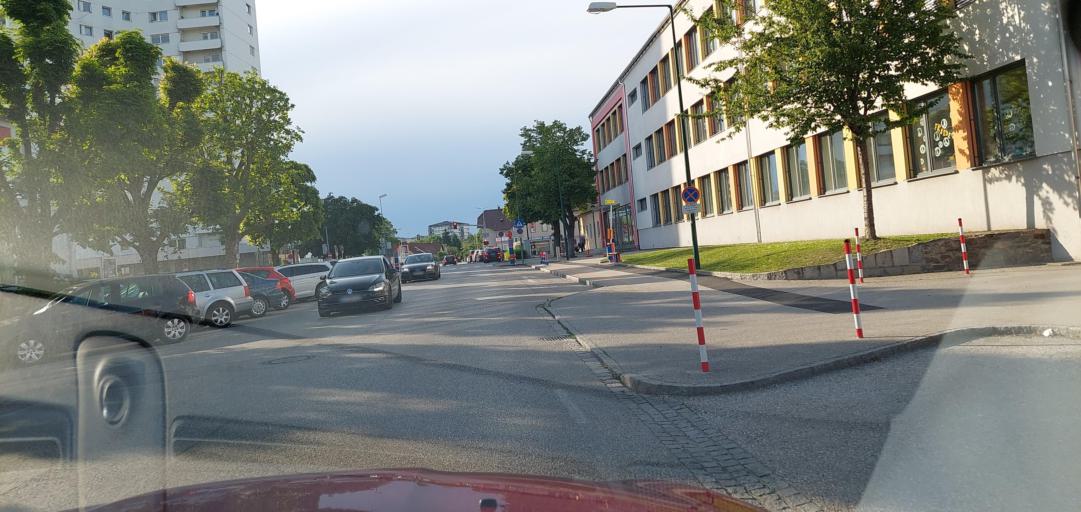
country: AT
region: Upper Austria
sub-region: Wels-Land
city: Thalheim bei Wels
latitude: 48.1553
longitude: 14.0041
